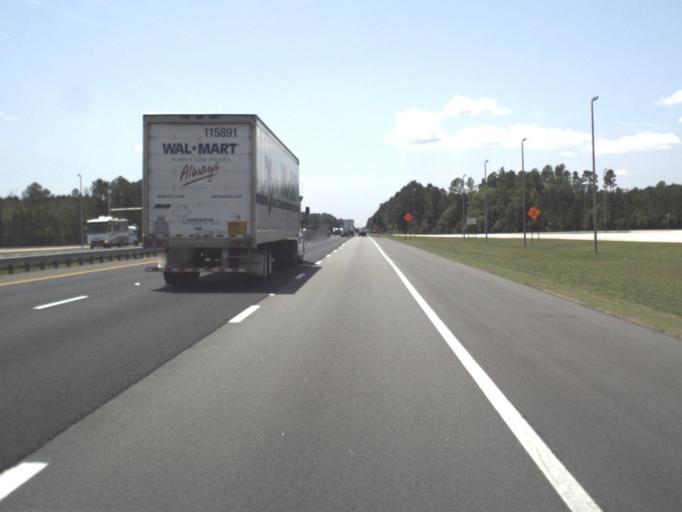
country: US
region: Florida
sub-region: Nassau County
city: Yulee
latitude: 30.6691
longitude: -81.6676
